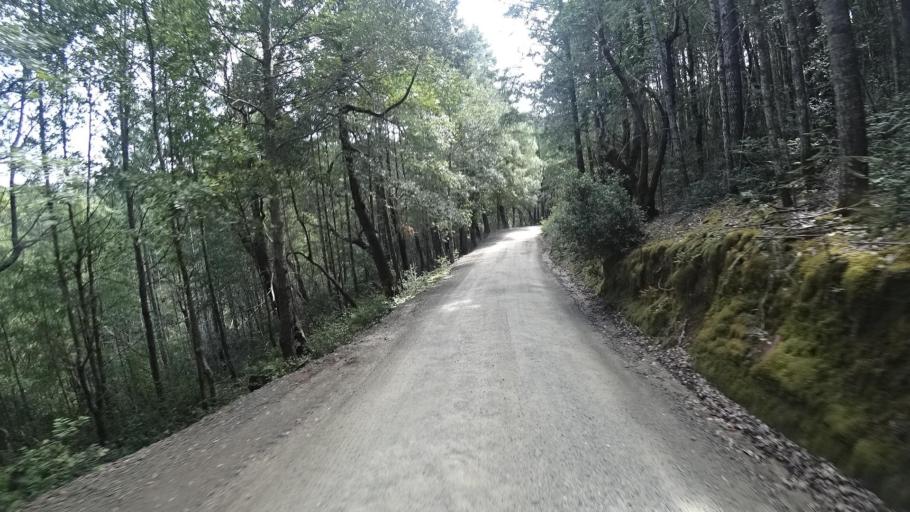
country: US
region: California
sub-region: Humboldt County
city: Redway
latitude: 40.0296
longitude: -123.8402
